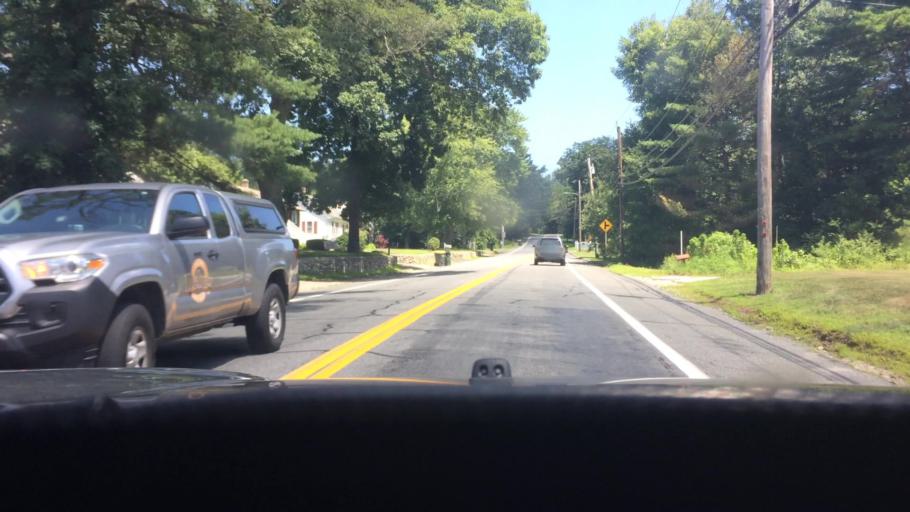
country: US
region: Rhode Island
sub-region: Providence County
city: Harrisville
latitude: 41.9694
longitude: -71.6625
